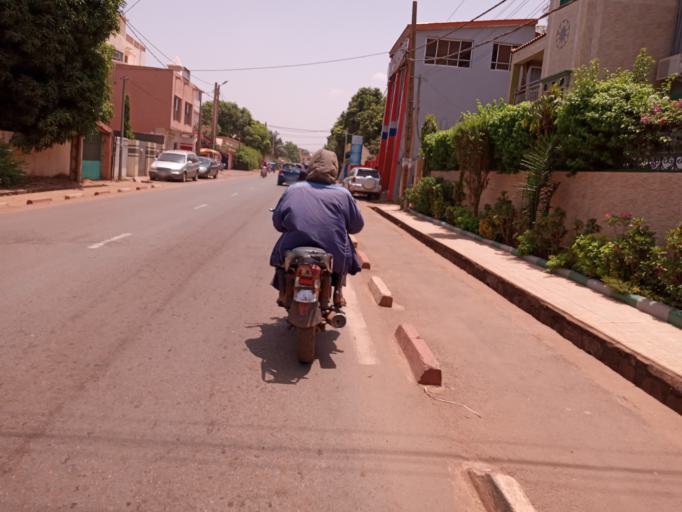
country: ML
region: Bamako
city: Bamako
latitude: 12.6450
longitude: -7.9772
